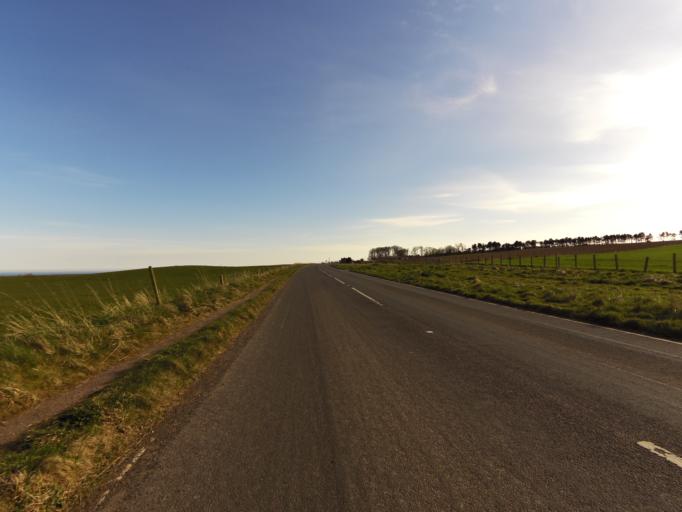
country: GB
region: Scotland
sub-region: Aberdeenshire
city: Stonehaven
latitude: 56.9492
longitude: -2.2051
